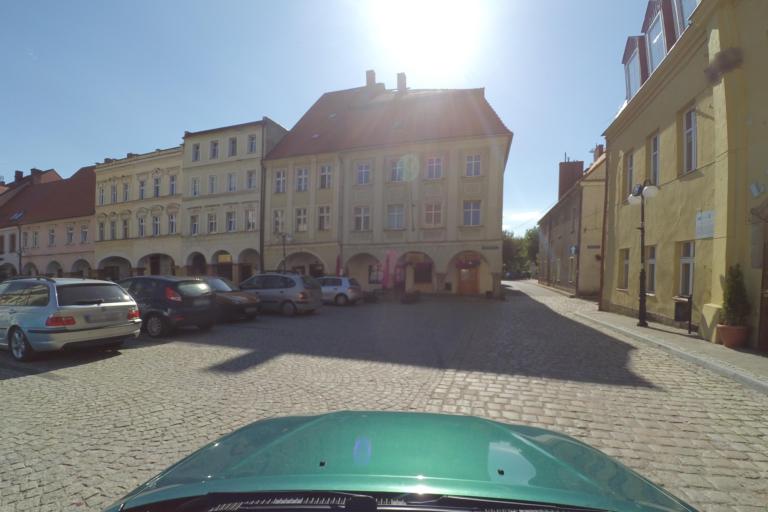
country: PL
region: Lower Silesian Voivodeship
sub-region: Powiat kamiennogorski
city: Lubawka
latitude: 50.7072
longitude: 16.0005
